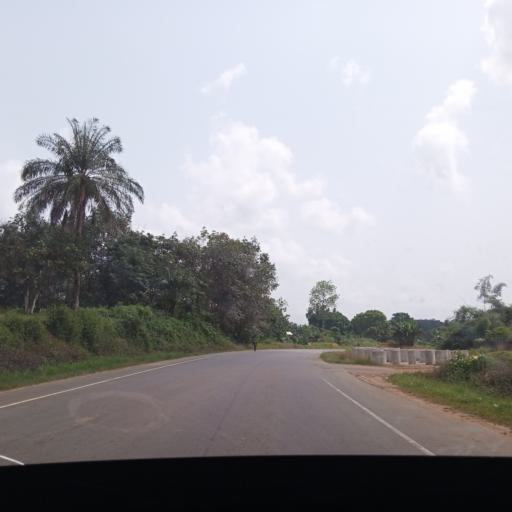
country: LR
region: Margibi
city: Kakata
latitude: 6.2503
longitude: -10.2967
